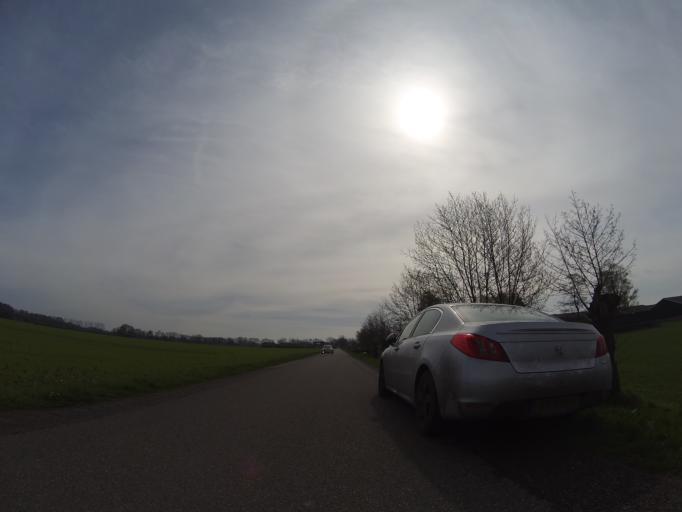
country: NL
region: Gelderland
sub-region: Gemeente Barneveld
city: Voorthuizen
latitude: 52.1889
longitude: 5.5695
